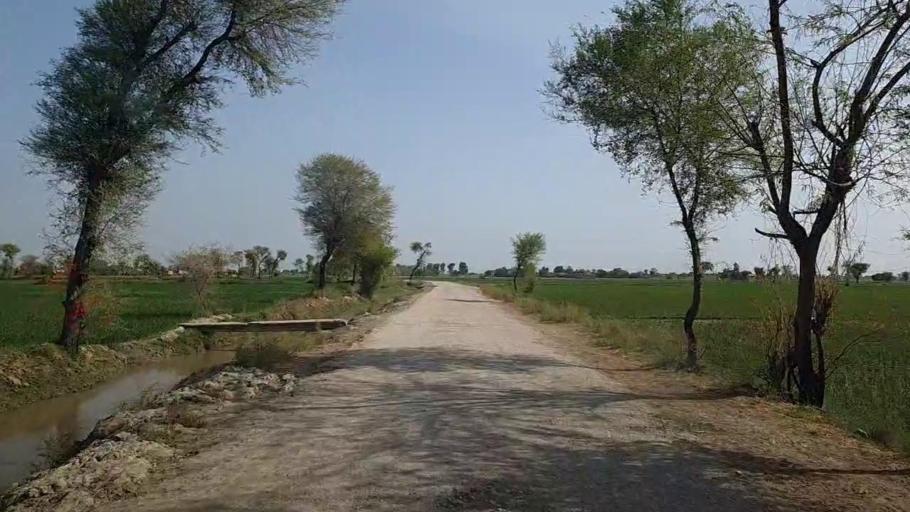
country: PK
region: Sindh
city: Sita Road
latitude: 27.1006
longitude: 67.8524
